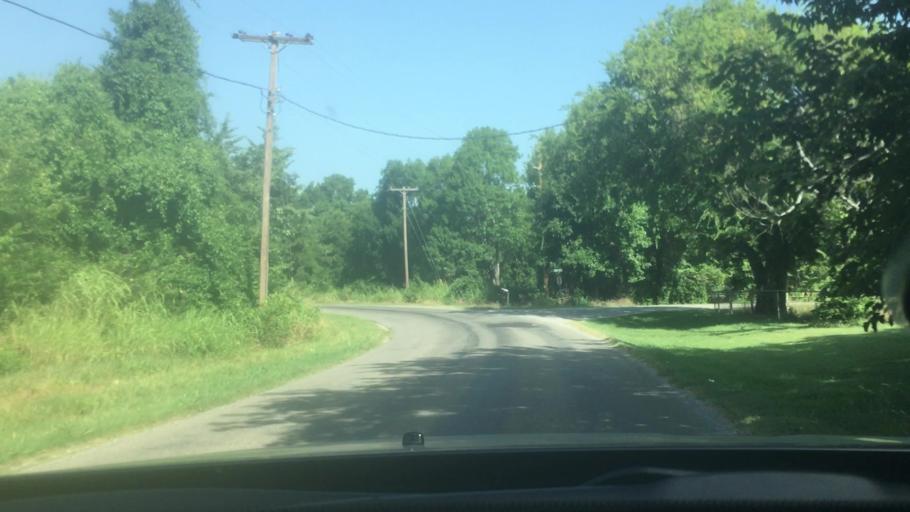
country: US
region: Oklahoma
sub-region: Bryan County
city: Calera
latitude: 33.9394
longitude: -96.4328
